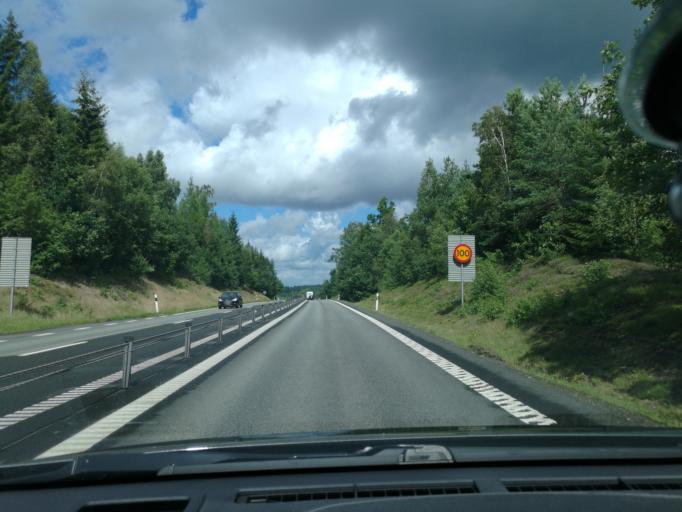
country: SE
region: Skane
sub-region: Osby Kommun
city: Osby
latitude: 56.3822
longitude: 14.0374
